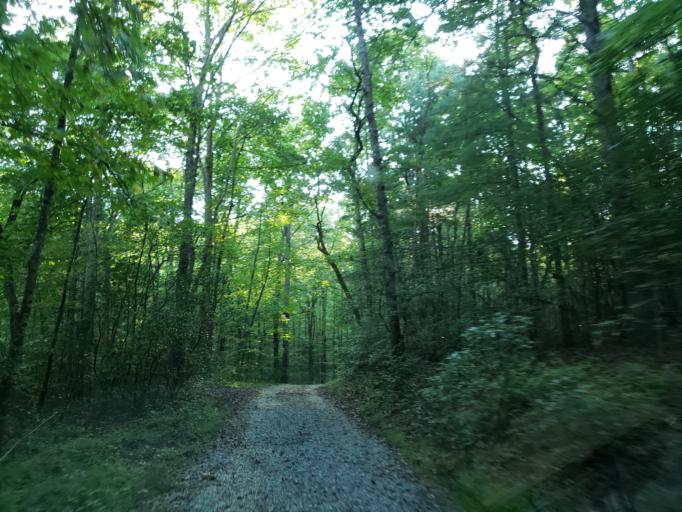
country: US
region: Georgia
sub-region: Fannin County
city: Blue Ridge
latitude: 34.7012
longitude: -84.2660
